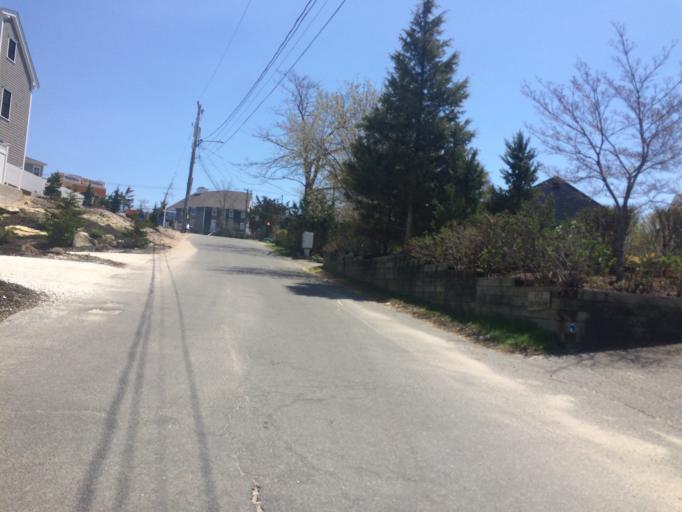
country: US
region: Massachusetts
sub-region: Barnstable County
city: Provincetown
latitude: 42.0437
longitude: -70.1970
